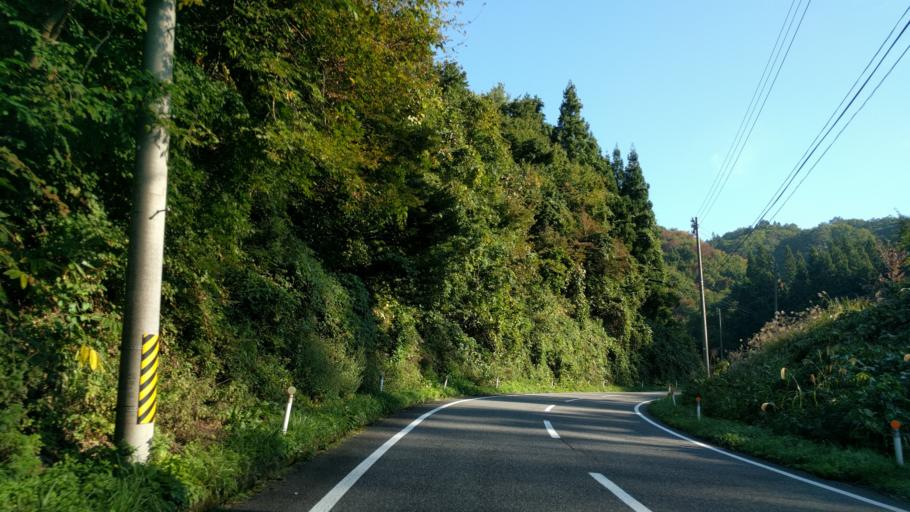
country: JP
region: Fukushima
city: Kitakata
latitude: 37.5057
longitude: 139.7417
